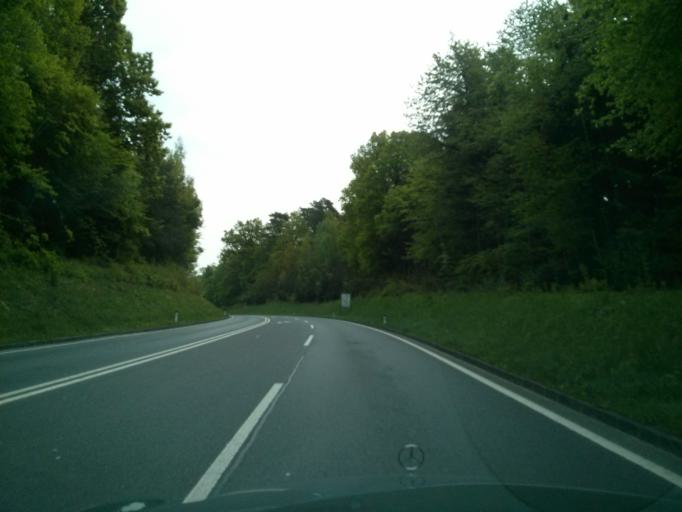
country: AT
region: Burgenland
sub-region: Politischer Bezirk Oberwart
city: Oberwart
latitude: 47.2796
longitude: 16.1665
